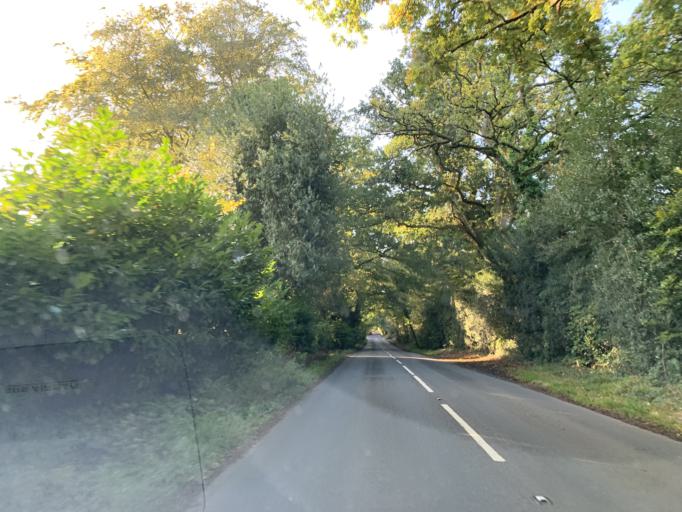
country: GB
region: England
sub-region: Hampshire
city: West Wellow
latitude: 50.9590
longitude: -1.6310
